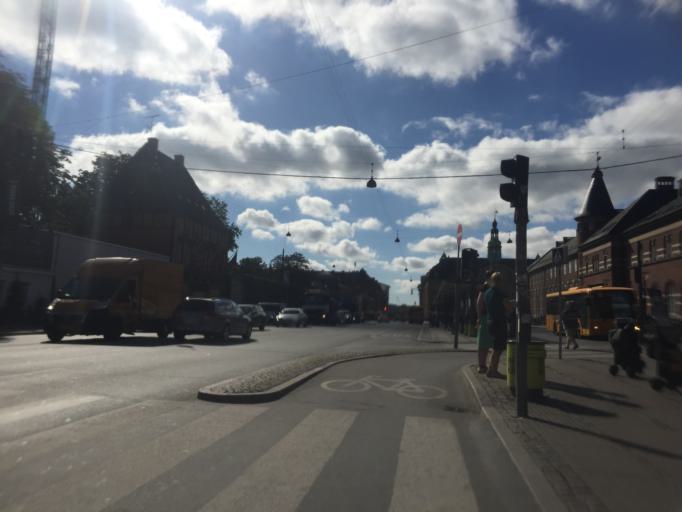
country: DK
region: Capital Region
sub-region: Kobenhavn
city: Copenhagen
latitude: 55.6732
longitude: 12.5661
